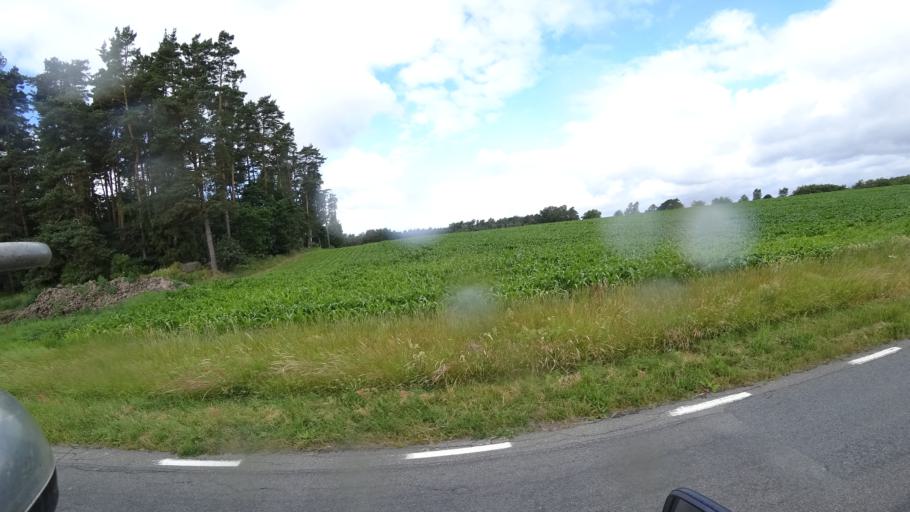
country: SE
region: Skane
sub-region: Kristianstads Kommun
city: Degeberga
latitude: 55.9098
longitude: 14.0159
